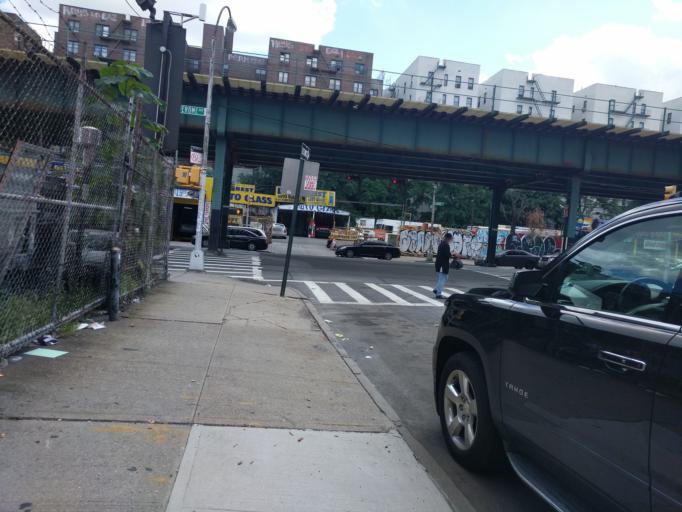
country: US
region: New York
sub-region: New York County
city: Inwood
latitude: 40.8434
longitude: -73.9158
